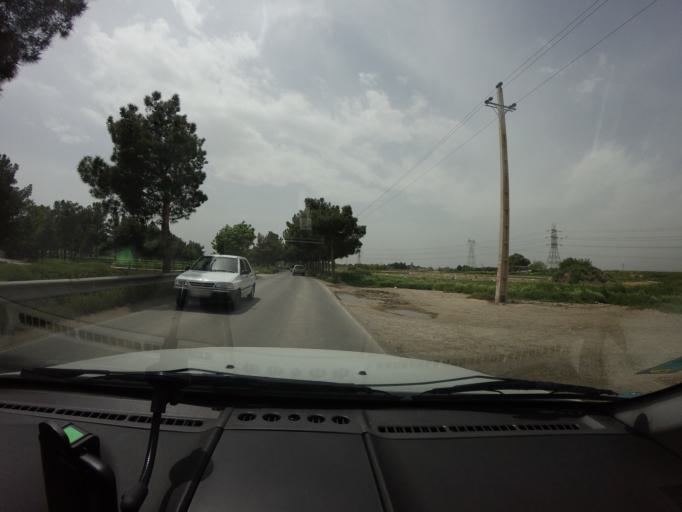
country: IR
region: Tehran
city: Eslamshahr
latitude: 35.5325
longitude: 51.2847
